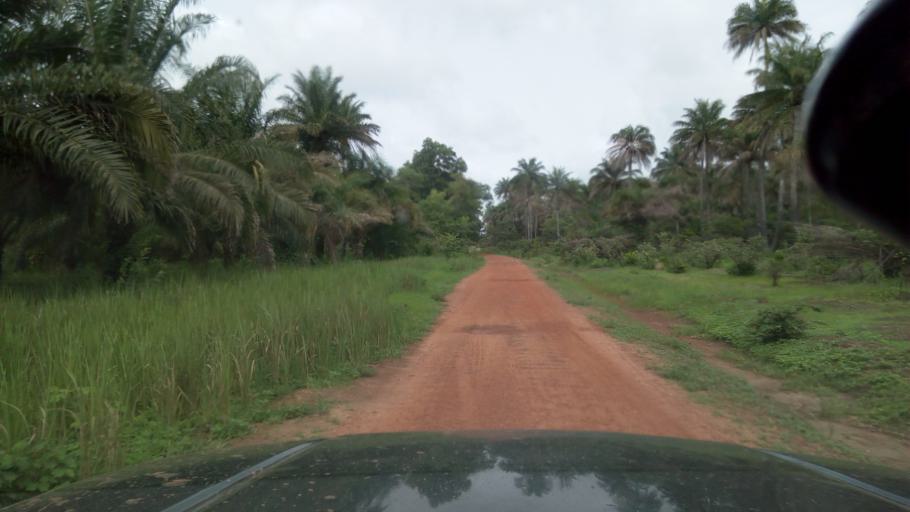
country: SL
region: Northern Province
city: Mange
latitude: 8.8352
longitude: -12.9410
